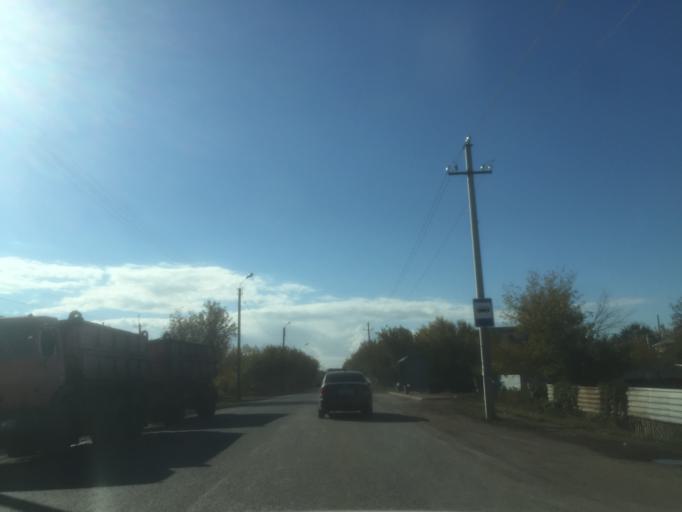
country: KZ
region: Astana Qalasy
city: Astana
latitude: 51.1936
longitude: 71.3470
